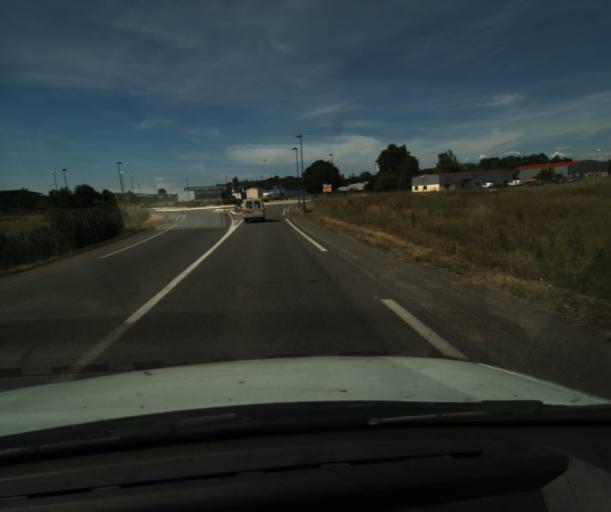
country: FR
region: Midi-Pyrenees
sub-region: Departement du Tarn-et-Garonne
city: Moissac
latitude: 44.1056
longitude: 1.1135
